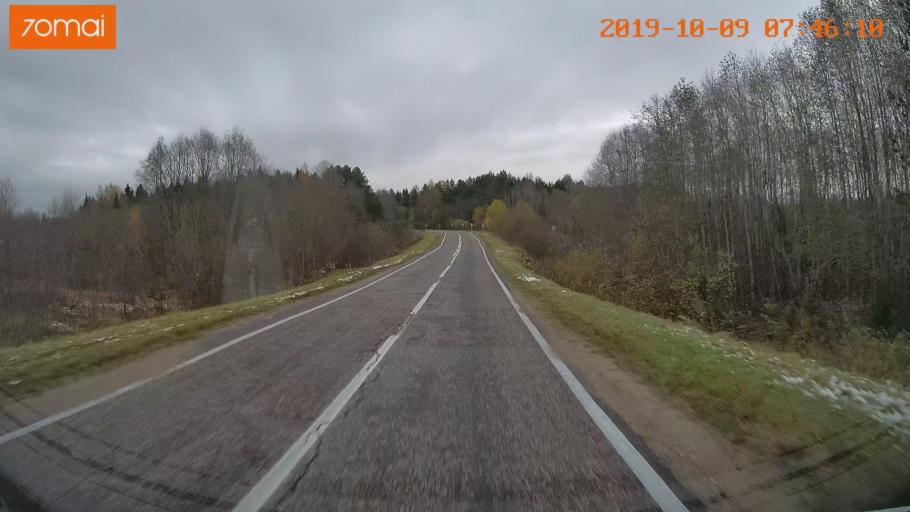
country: RU
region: Jaroslavl
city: Kukoboy
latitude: 58.6557
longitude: 39.7823
